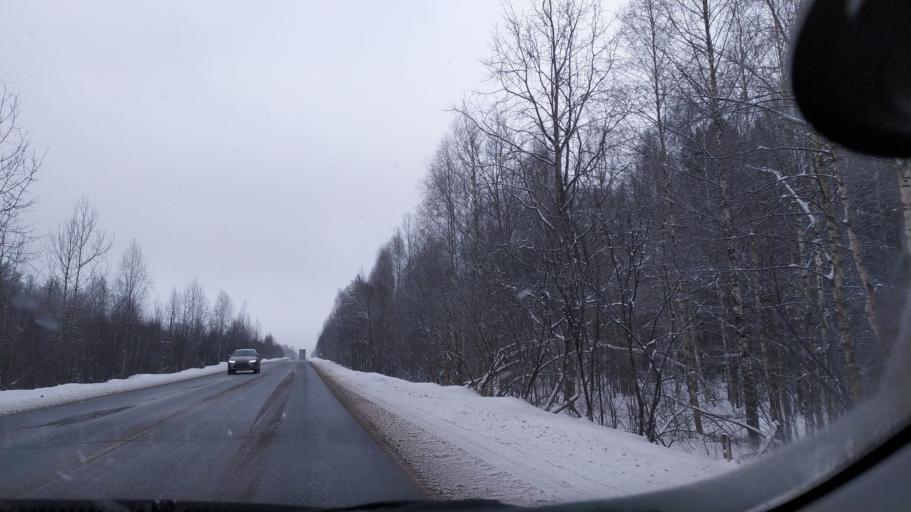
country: RU
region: Mariy-El
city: Krasnogorskiy
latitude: 56.1655
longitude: 48.2150
